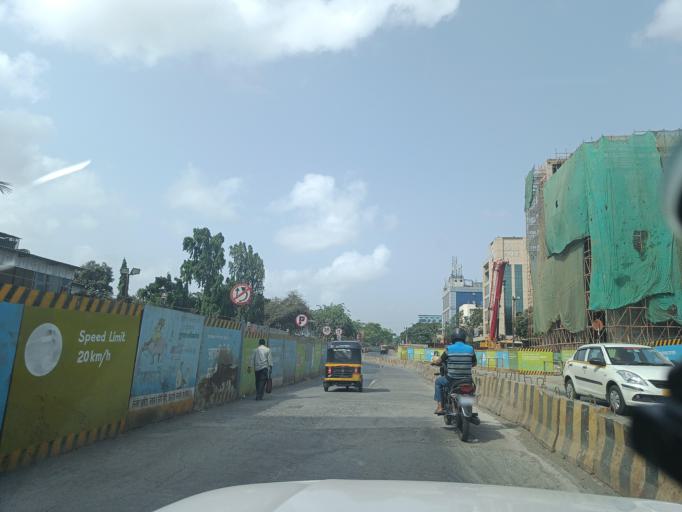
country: IN
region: Maharashtra
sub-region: Mumbai Suburban
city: Powai
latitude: 19.1263
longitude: 72.8738
